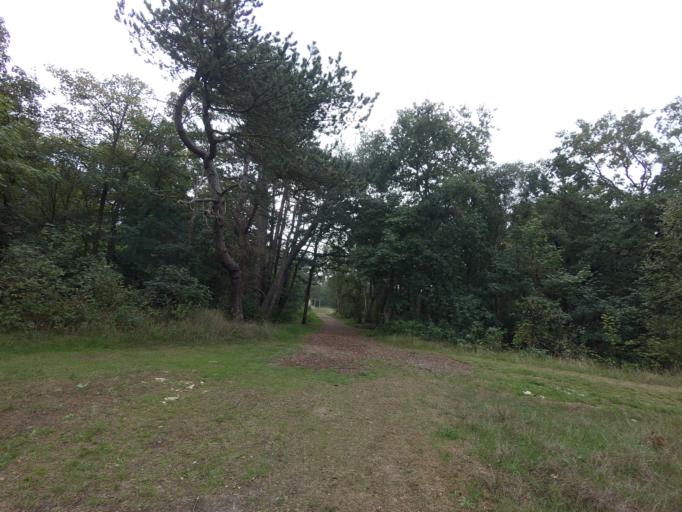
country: NL
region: Friesland
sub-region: Gemeente Schiermonnikoog
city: Schiermonnikoog
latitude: 53.4853
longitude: 6.1663
